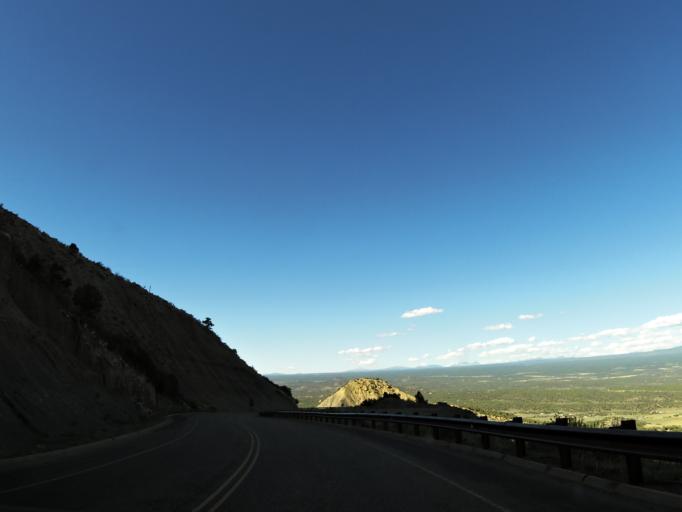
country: US
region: Colorado
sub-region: Montezuma County
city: Mancos
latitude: 37.3150
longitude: -108.4150
